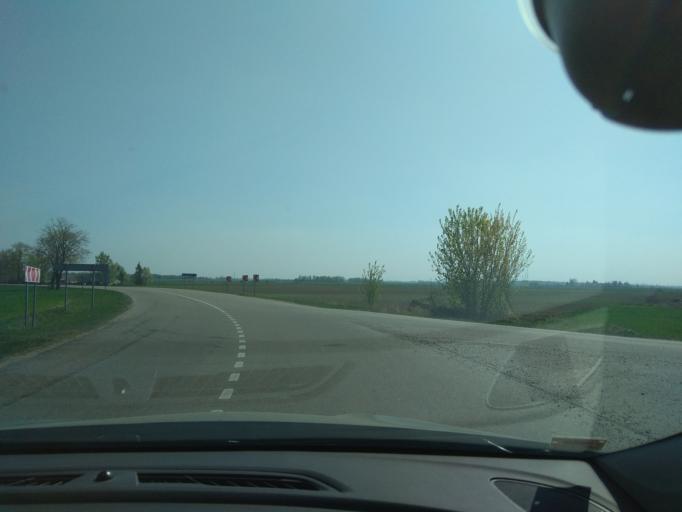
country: LT
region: Panevezys
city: Pasvalys
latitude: 55.9443
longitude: 24.2132
